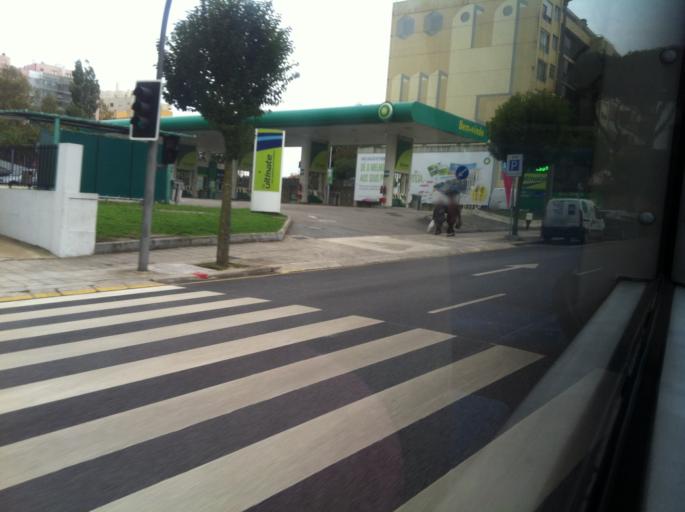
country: PT
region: Porto
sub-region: Porto
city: Porto
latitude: 41.1634
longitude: -8.6337
